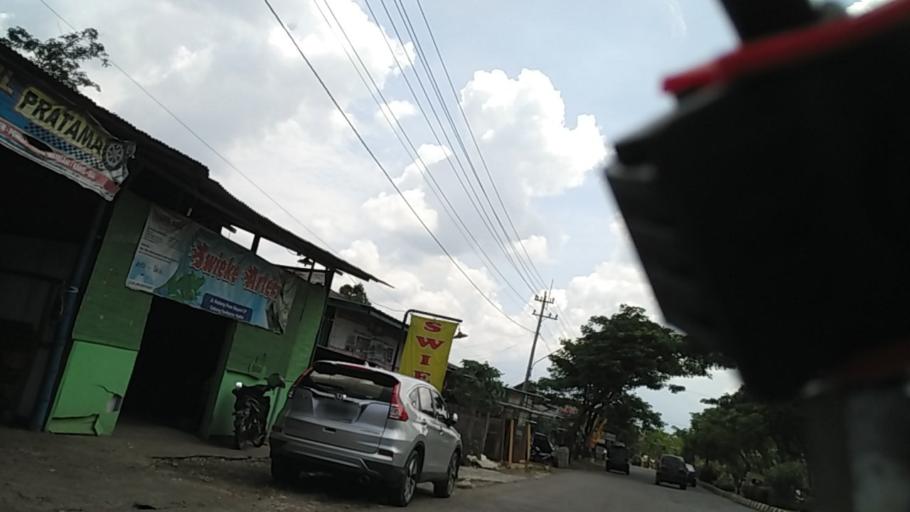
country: ID
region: Central Java
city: Semarang
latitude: -7.0151
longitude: 110.3385
